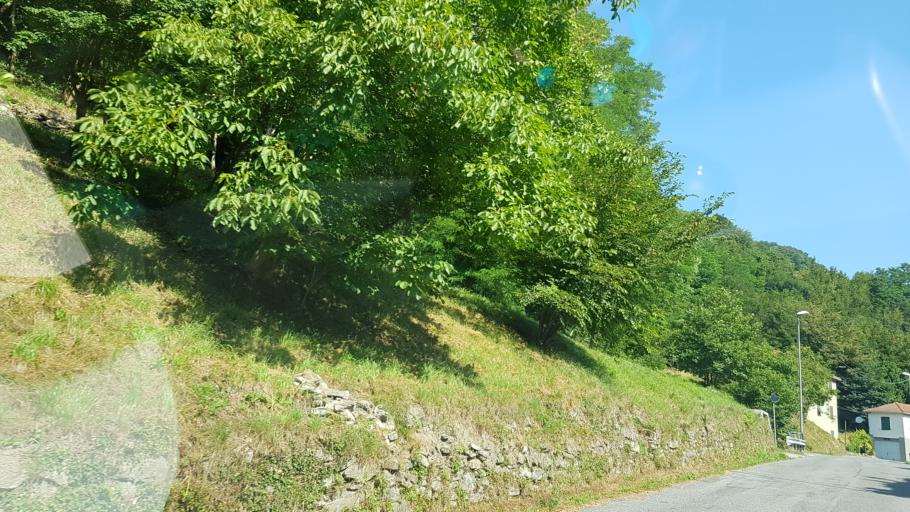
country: IT
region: Liguria
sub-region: Provincia di Genova
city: Serra Ricco
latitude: 44.5179
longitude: 8.9396
